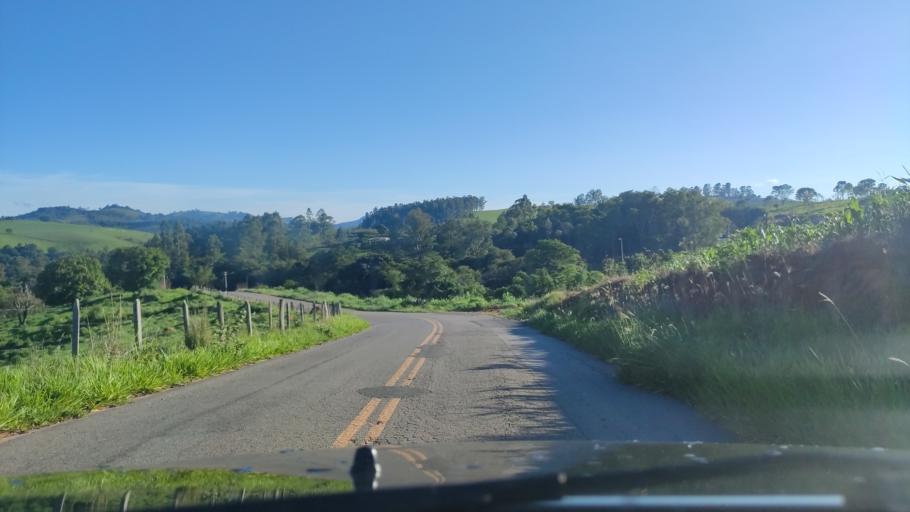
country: BR
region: Sao Paulo
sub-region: Aguas De Lindoia
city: Aguas de Lindoia
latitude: -22.5520
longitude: -46.6140
